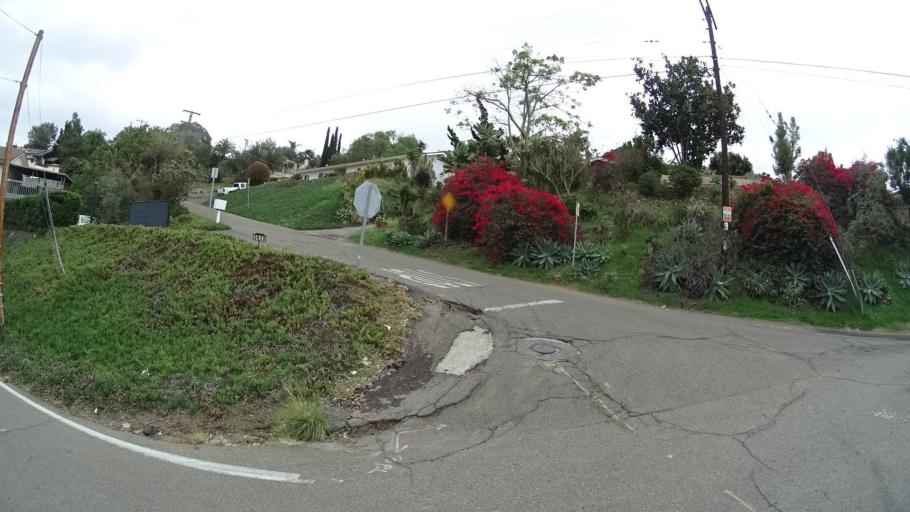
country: US
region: California
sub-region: San Diego County
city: Spring Valley
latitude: 32.7483
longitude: -116.9993
